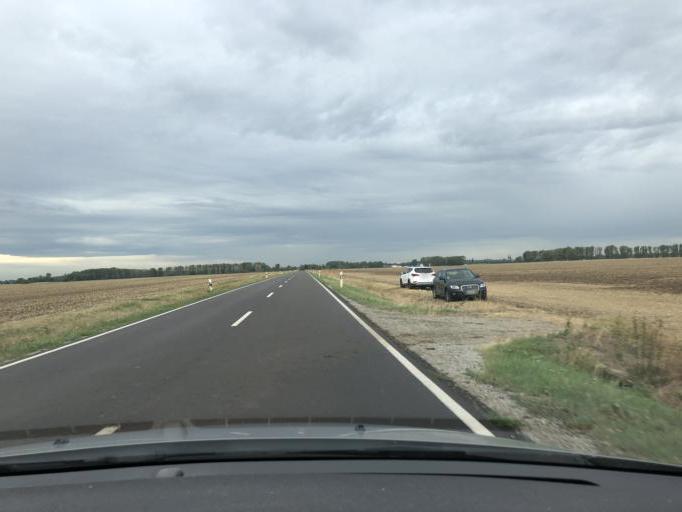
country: DE
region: Saxony-Anhalt
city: Calbe
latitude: 51.8858
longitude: 11.8236
